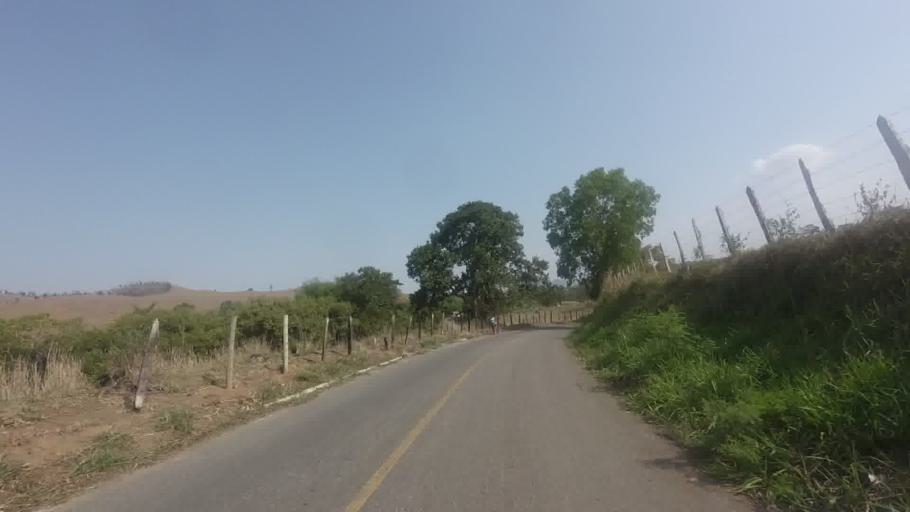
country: BR
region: Rio de Janeiro
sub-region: Bom Jesus Do Itabapoana
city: Bom Jesus do Itabapoana
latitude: -21.1428
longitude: -41.5689
